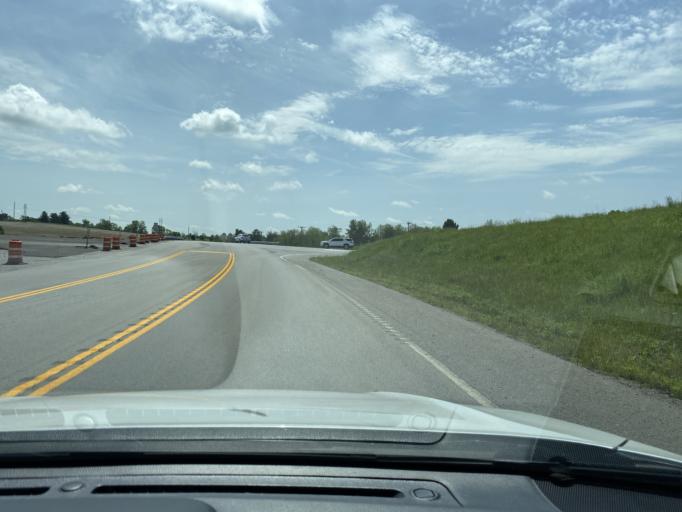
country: US
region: Kentucky
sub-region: Scott County
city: Georgetown
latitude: 38.2431
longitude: -84.5835
